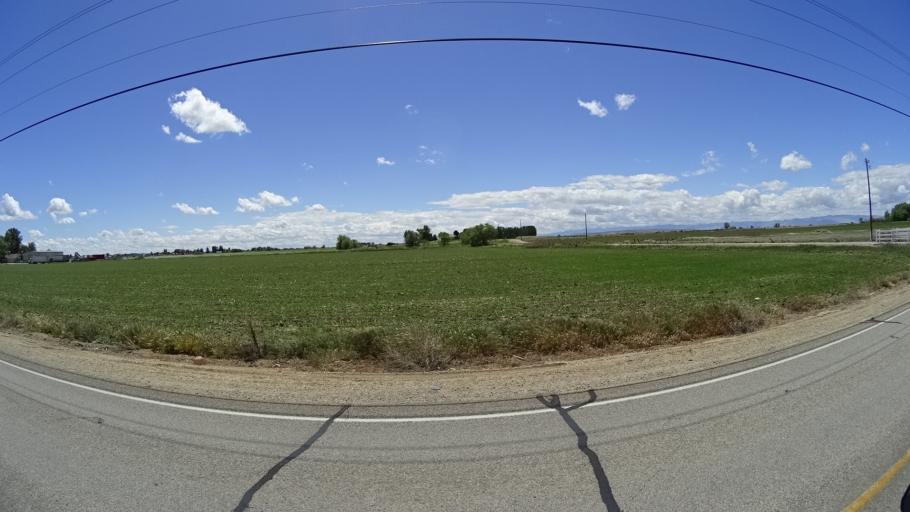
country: US
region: Idaho
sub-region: Ada County
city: Meridian
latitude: 43.5465
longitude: -116.3786
